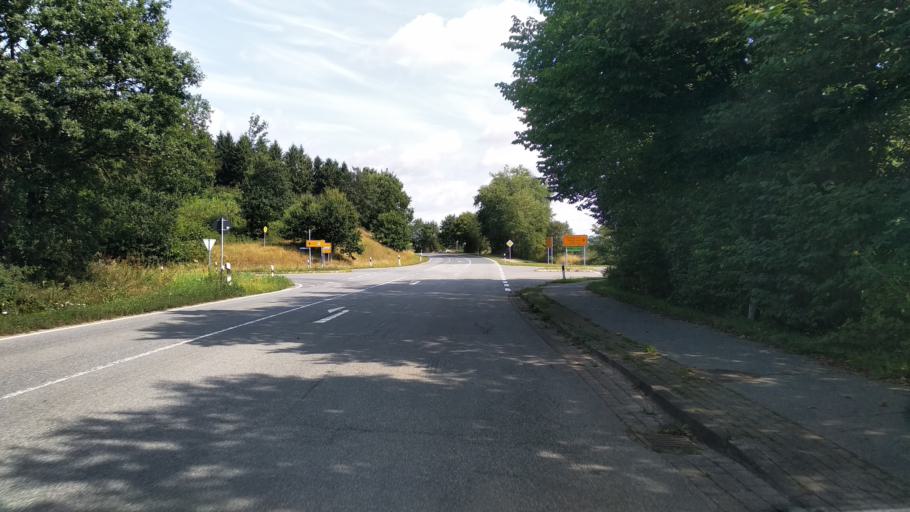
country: DE
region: Schleswig-Holstein
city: Selk
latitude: 54.4760
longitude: 9.5658
